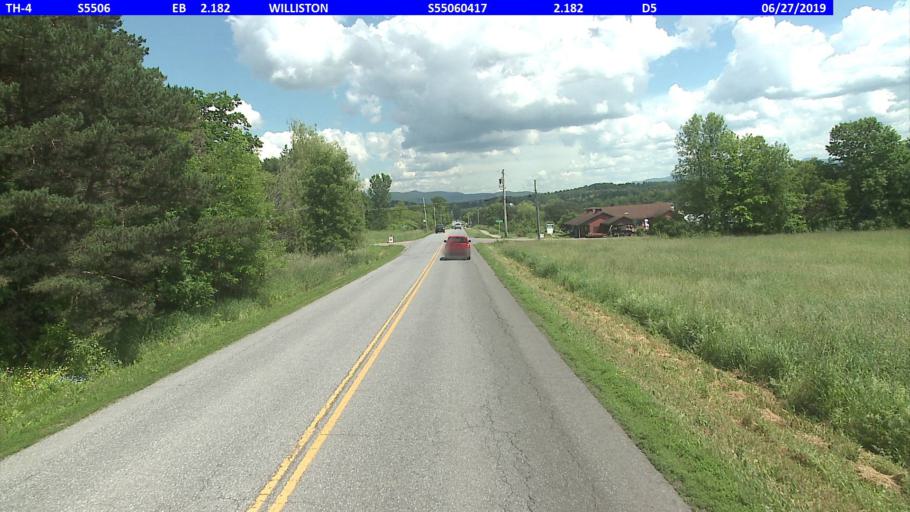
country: US
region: Vermont
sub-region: Chittenden County
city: Williston
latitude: 44.4545
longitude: -73.0739
